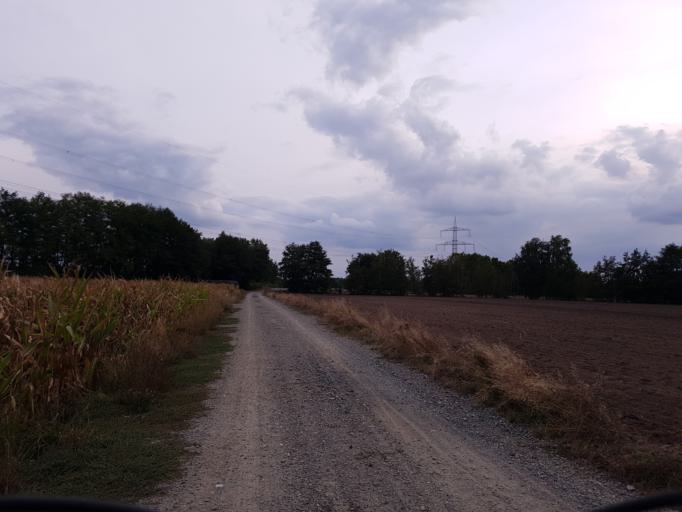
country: DE
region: Brandenburg
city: Trobitz
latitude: 51.5467
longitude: 13.4449
